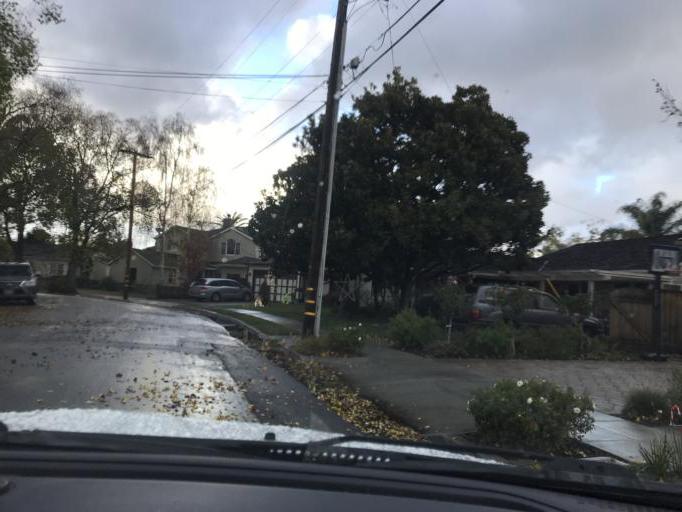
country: US
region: California
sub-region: Santa Clara County
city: Buena Vista
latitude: 37.3087
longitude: -121.9031
